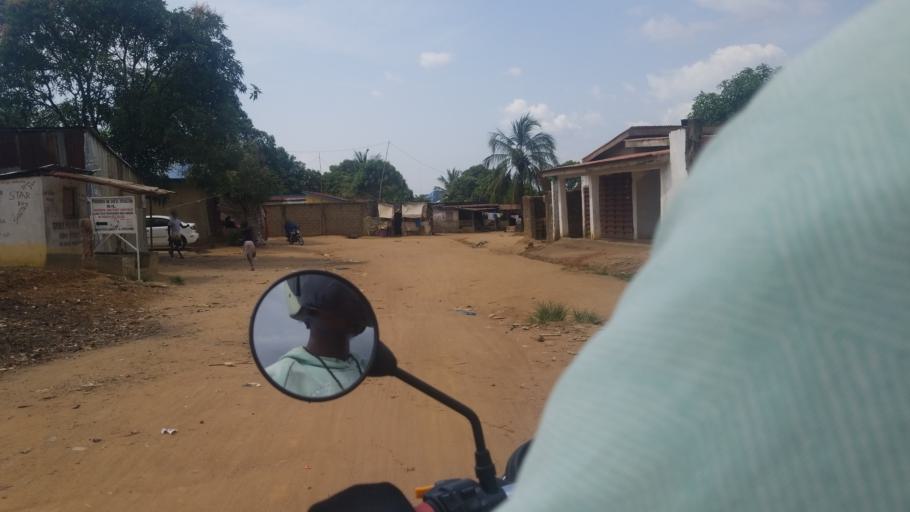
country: SL
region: Western Area
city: Waterloo
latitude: 8.3212
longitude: -13.0471
